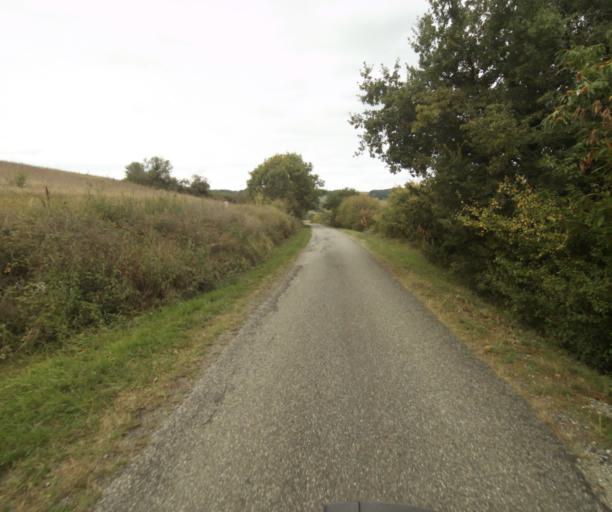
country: FR
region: Midi-Pyrenees
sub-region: Departement du Tarn-et-Garonne
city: Beaumont-de-Lomagne
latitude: 43.8450
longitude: 1.0915
